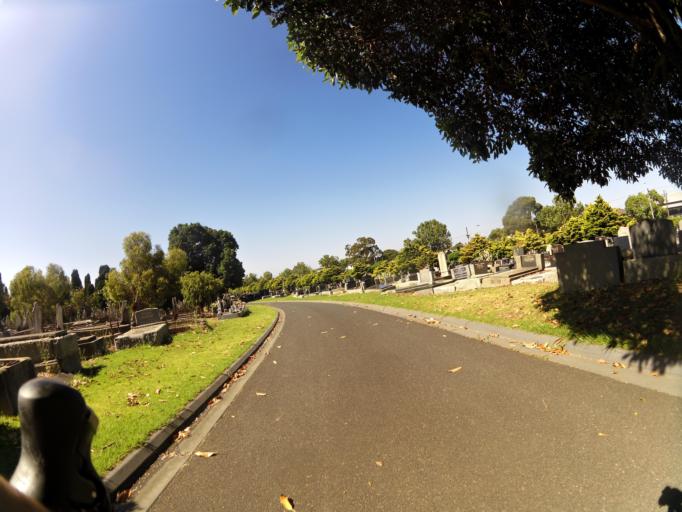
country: AU
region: Victoria
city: Carlton
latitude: -37.7919
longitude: 144.9678
